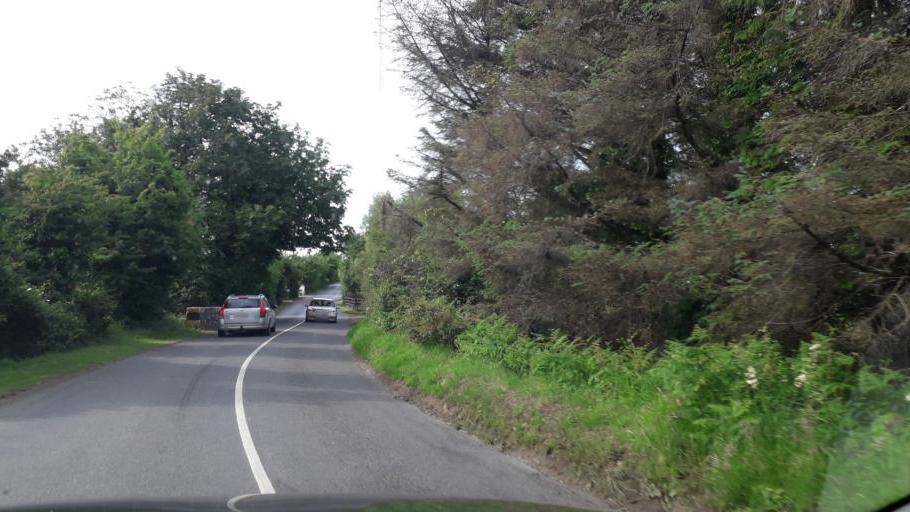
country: IE
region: Leinster
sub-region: Loch Garman
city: Courtown
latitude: 52.5693
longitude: -6.2303
